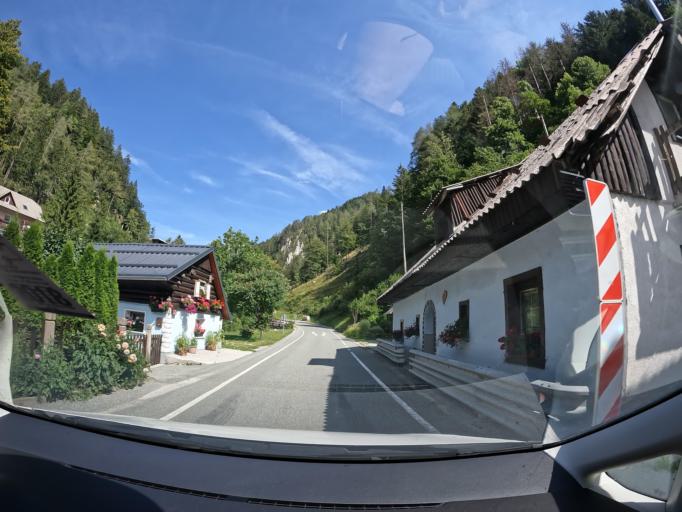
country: SI
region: Jesenice
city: Koroska Bela
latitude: 46.4613
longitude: 14.0886
